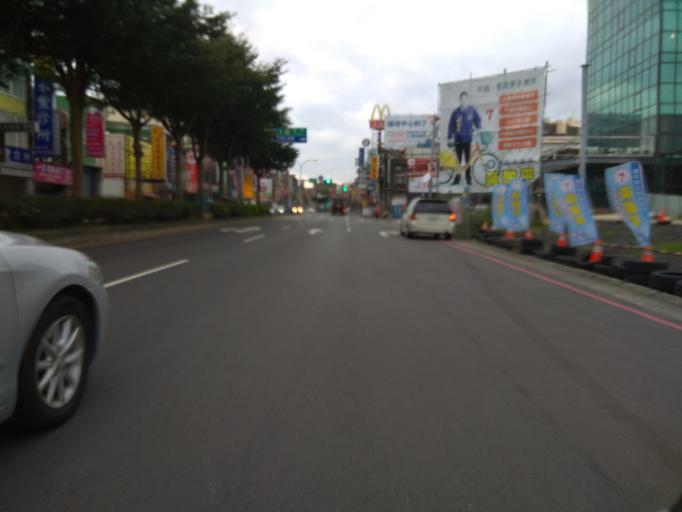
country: TW
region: Taiwan
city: Daxi
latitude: 24.9014
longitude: 121.2113
